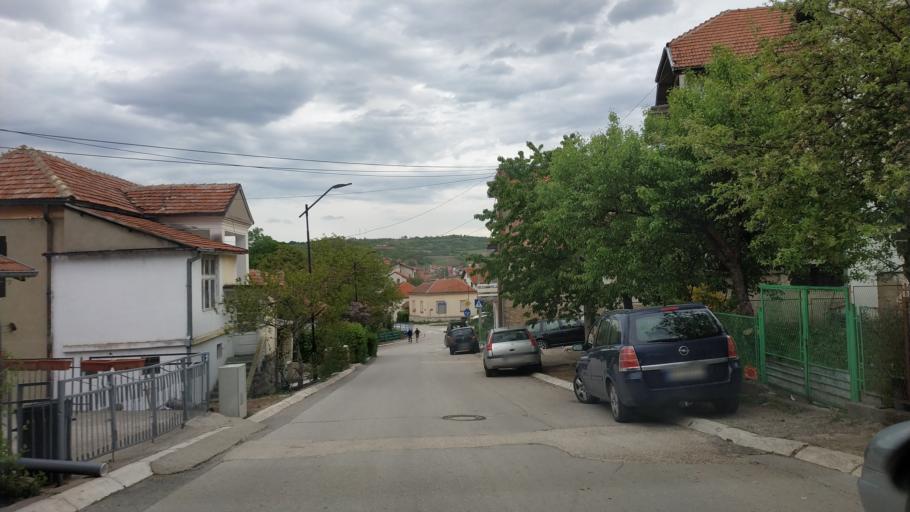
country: RS
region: Central Serbia
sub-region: Zajecarski Okrug
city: Soko Banja
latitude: 43.6417
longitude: 21.8713
